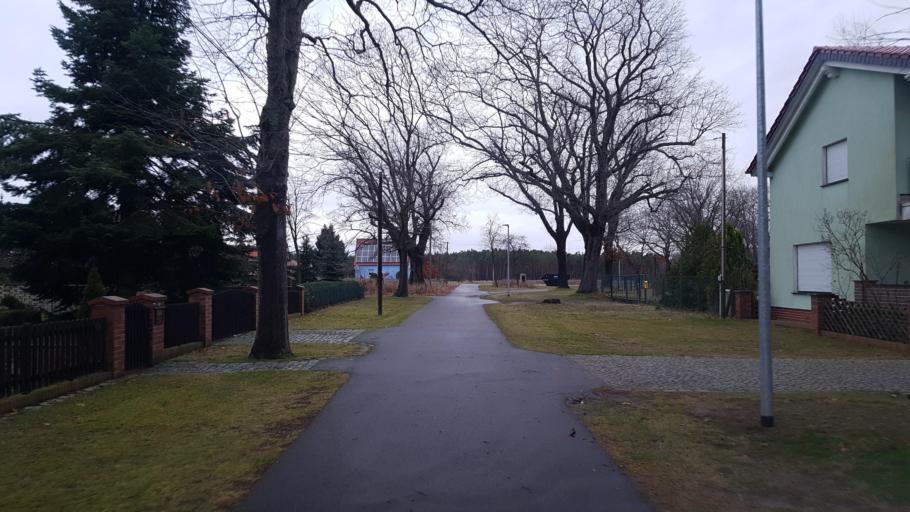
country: DE
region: Brandenburg
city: Tauche
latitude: 52.0704
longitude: 14.0978
